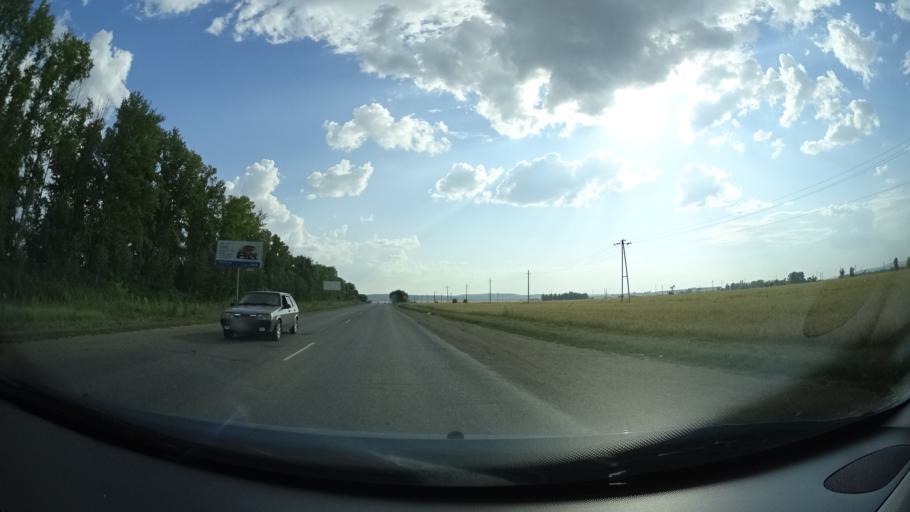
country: RU
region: Bashkortostan
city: Oktyabr'skiy
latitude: 54.4814
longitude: 53.4046
